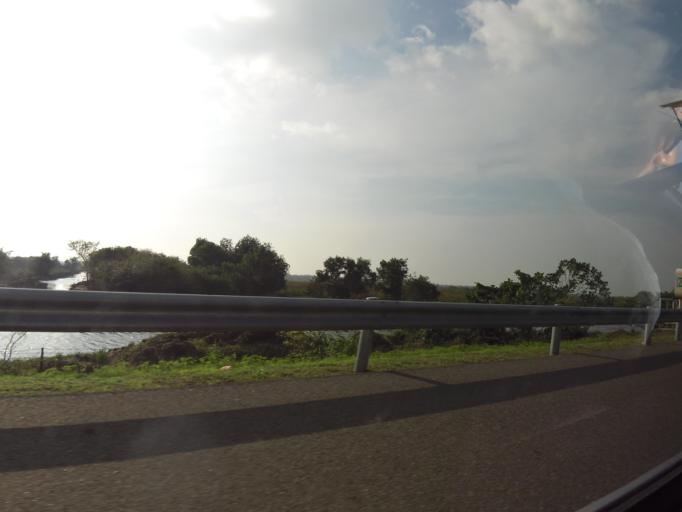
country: LK
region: Western
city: Kandana
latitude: 7.0525
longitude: 79.8803
